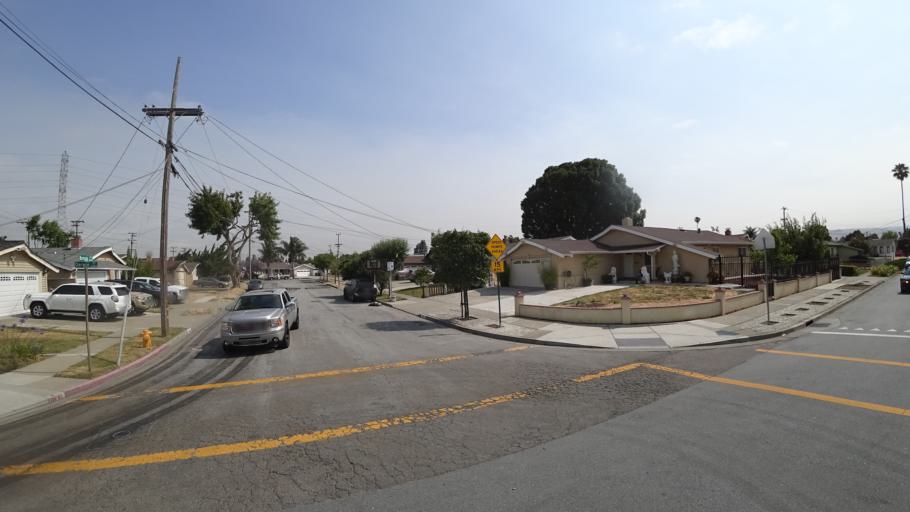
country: US
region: California
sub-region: Alameda County
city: Hayward
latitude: 37.6316
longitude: -122.1008
